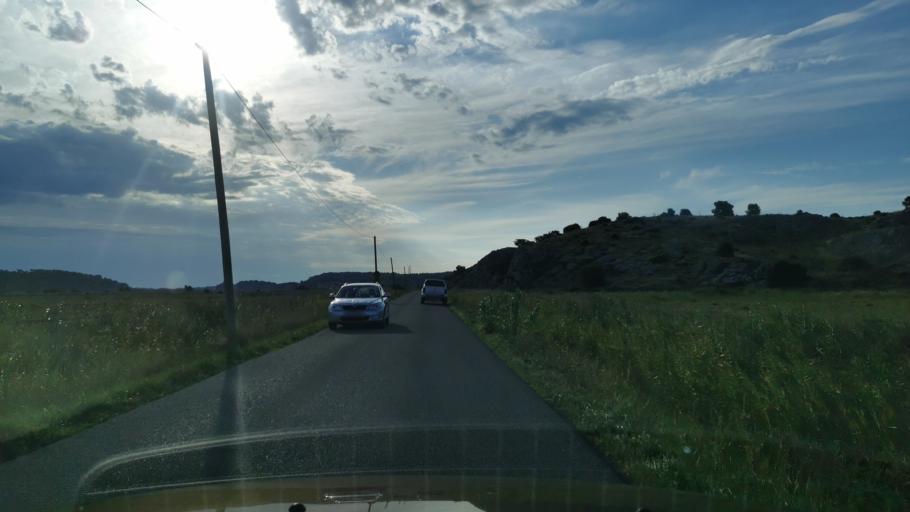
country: FR
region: Languedoc-Roussillon
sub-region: Departement de l'Aude
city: Gruissan
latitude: 43.1142
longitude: 3.0426
